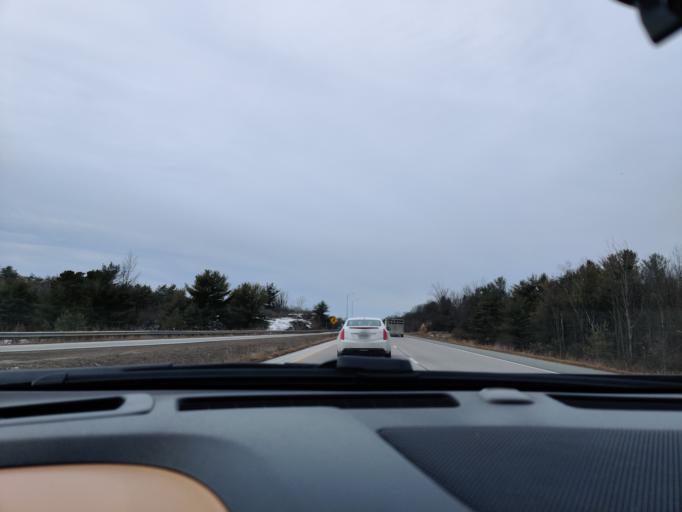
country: CA
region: Ontario
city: Gananoque
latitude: 44.3445
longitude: -76.1499
